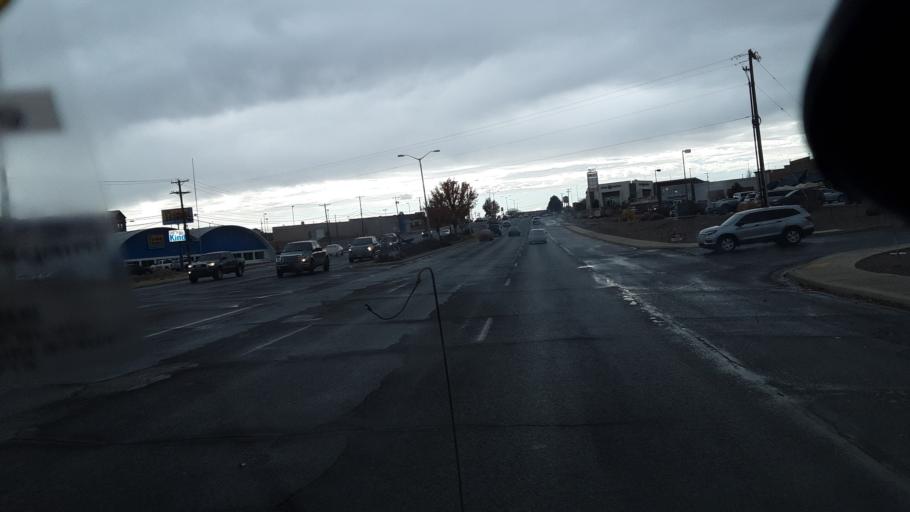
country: US
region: New Mexico
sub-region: San Juan County
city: Flora Vista
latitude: 36.7696
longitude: -108.1433
